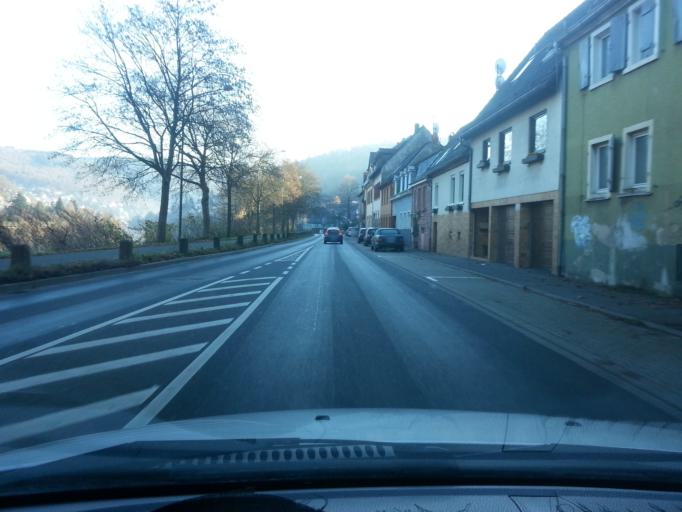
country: DE
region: Baden-Wuerttemberg
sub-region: Karlsruhe Region
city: Heidelberg
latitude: 49.4162
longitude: 8.7398
